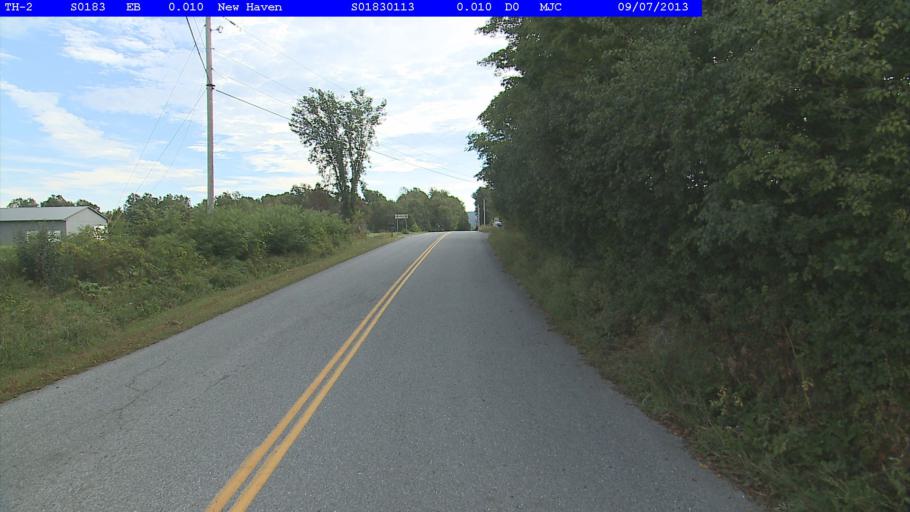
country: US
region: Vermont
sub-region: Addison County
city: Middlebury (village)
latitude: 44.0555
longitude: -73.1673
